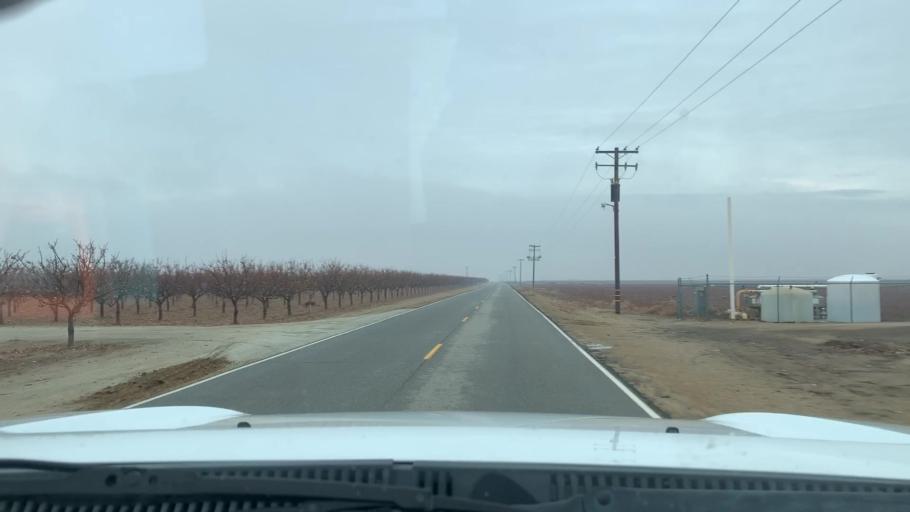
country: US
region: California
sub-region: Kern County
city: Lost Hills
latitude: 35.6264
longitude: -119.5801
